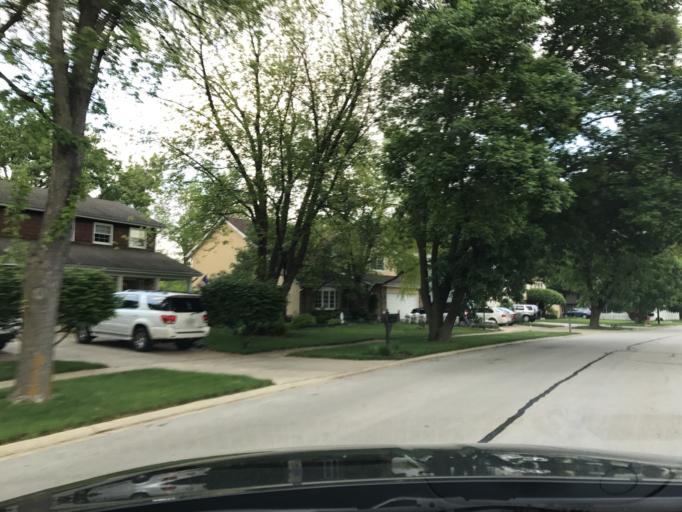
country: US
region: Illinois
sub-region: DuPage County
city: Naperville
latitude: 41.7763
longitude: -88.1157
